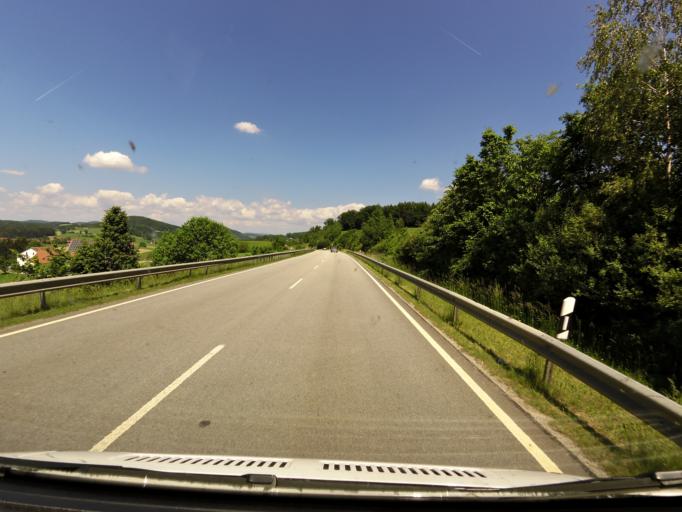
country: DE
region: Bavaria
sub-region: Lower Bavaria
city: Roehrnbach
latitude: 48.7649
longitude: 13.5100
